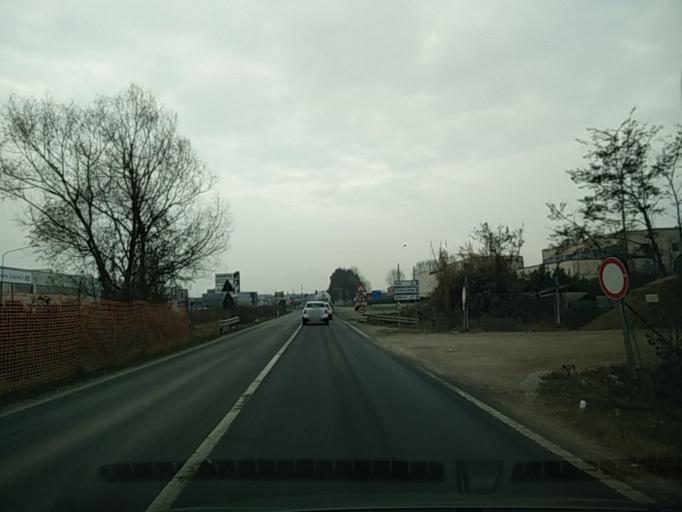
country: IT
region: Piedmont
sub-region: Provincia di Torino
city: Settimo Torinese
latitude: 45.1342
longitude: 7.7361
